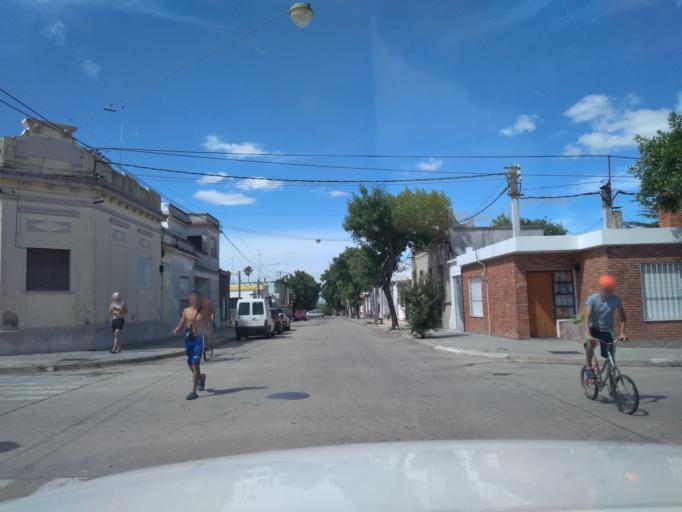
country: UY
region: Florida
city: Florida
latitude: -34.0958
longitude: -56.2127
